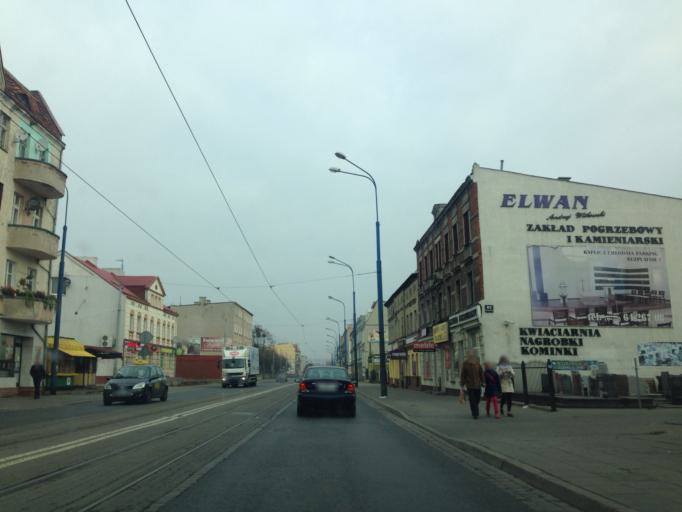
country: PL
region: Kujawsko-Pomorskie
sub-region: Grudziadz
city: Grudziadz
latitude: 53.4758
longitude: 18.7462
